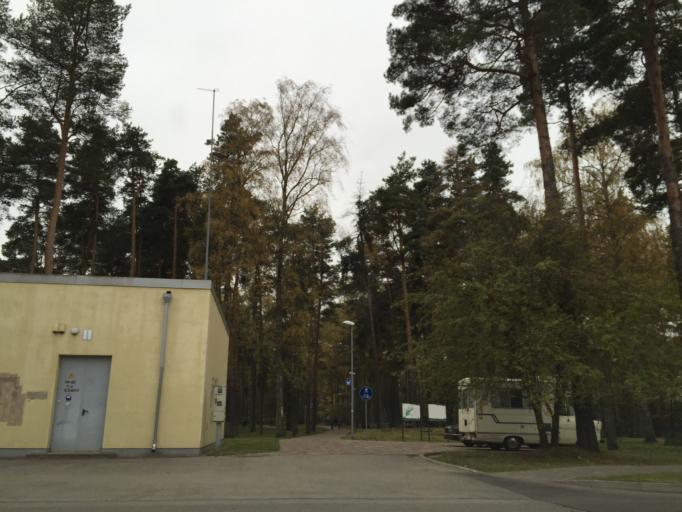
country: LV
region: Olaine
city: Olaine
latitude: 56.7854
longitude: 23.9358
